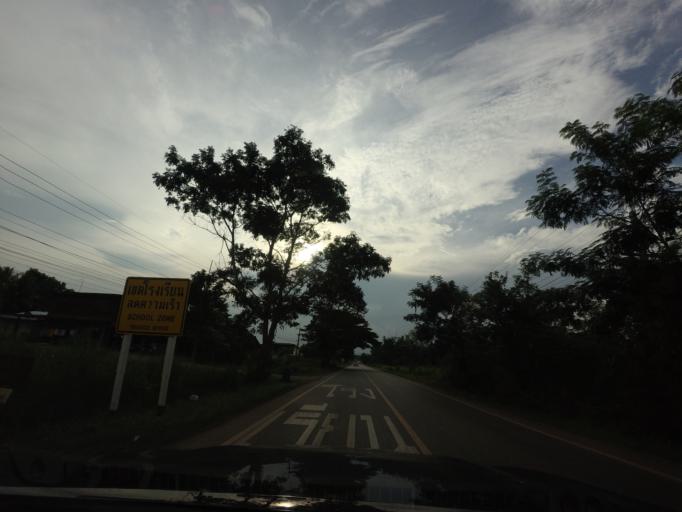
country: TH
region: Changwat Udon Thani
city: Nam Som
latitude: 17.8043
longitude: 102.2979
